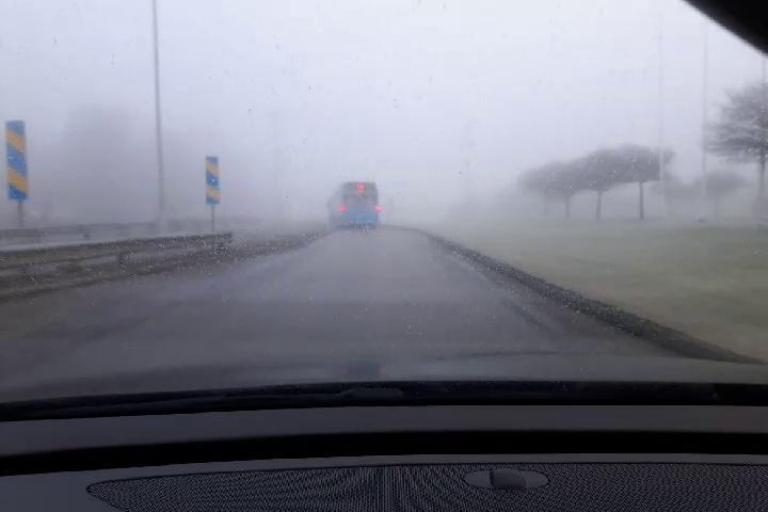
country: SE
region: Vaestra Goetaland
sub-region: Goteborg
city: Goeteborg
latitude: 57.7422
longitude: 11.9430
